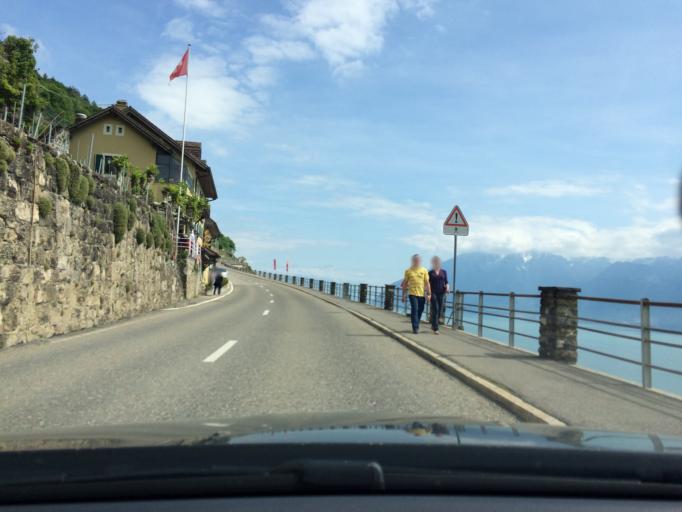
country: CH
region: Vaud
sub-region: Lavaux-Oron District
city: Chexbres
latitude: 46.4872
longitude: 6.7549
